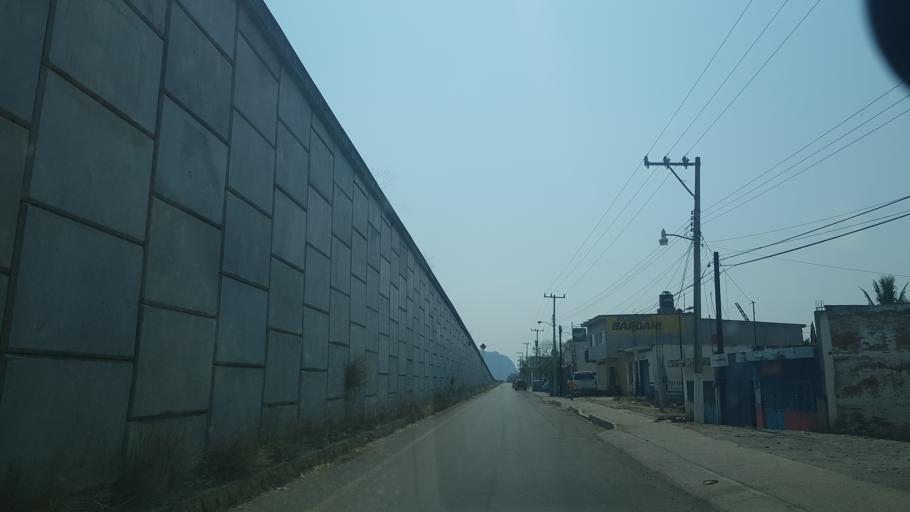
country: MX
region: Morelos
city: Amayuca
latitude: 18.7172
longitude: -98.7945
